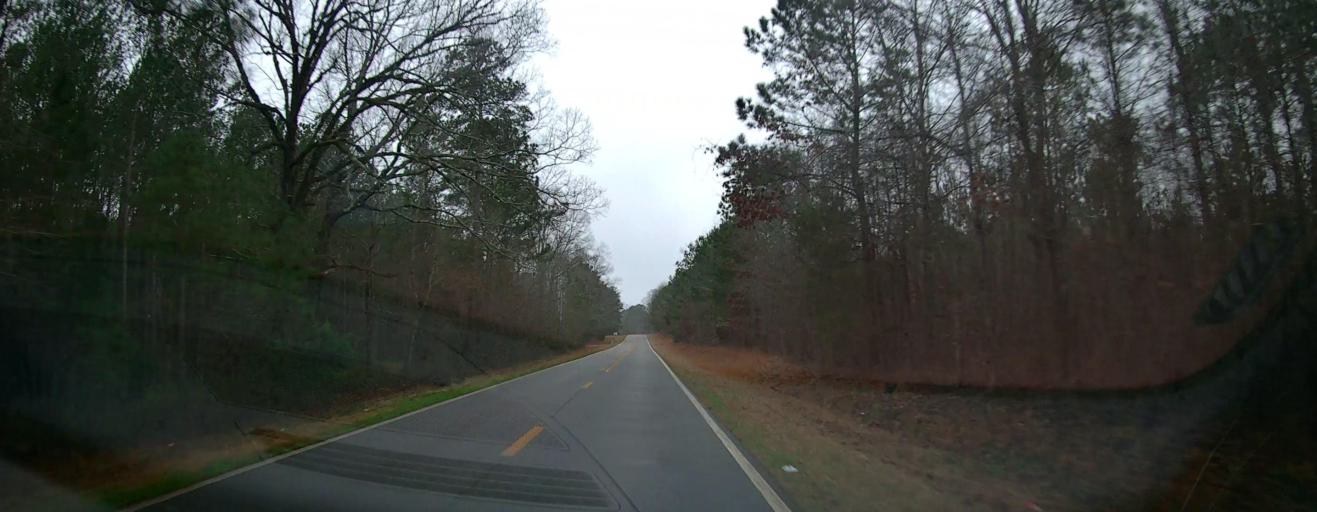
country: US
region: Georgia
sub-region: Monroe County
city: Forsyth
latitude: 33.1126
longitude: -84.0260
